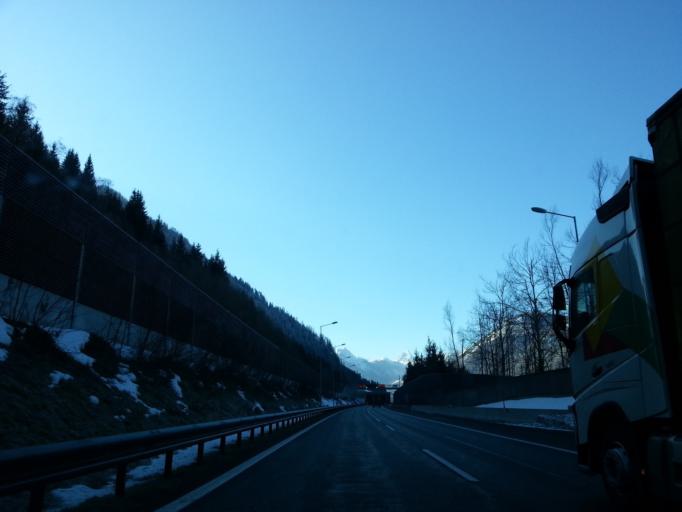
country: AT
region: Salzburg
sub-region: Politischer Bezirk Sankt Johann im Pongau
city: Flachau
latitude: 47.3493
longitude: 13.3971
